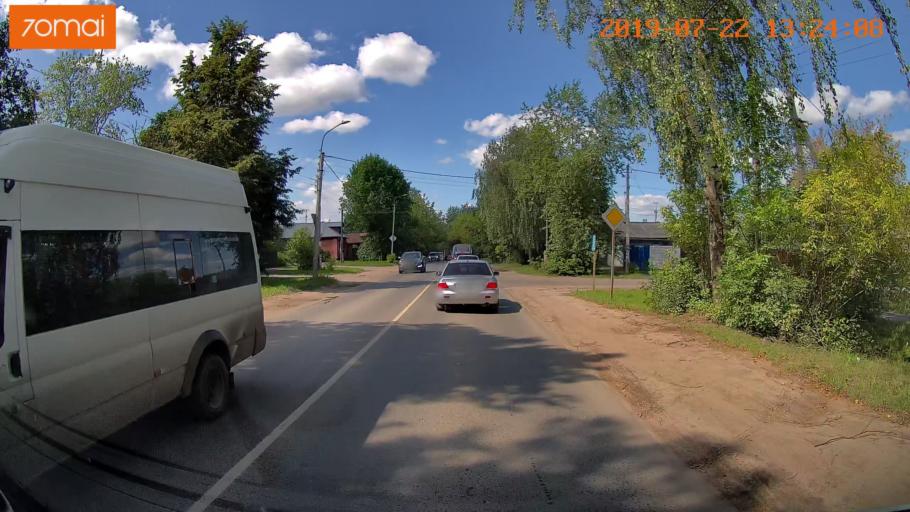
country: RU
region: Ivanovo
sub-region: Gorod Ivanovo
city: Ivanovo
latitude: 57.0263
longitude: 40.9521
